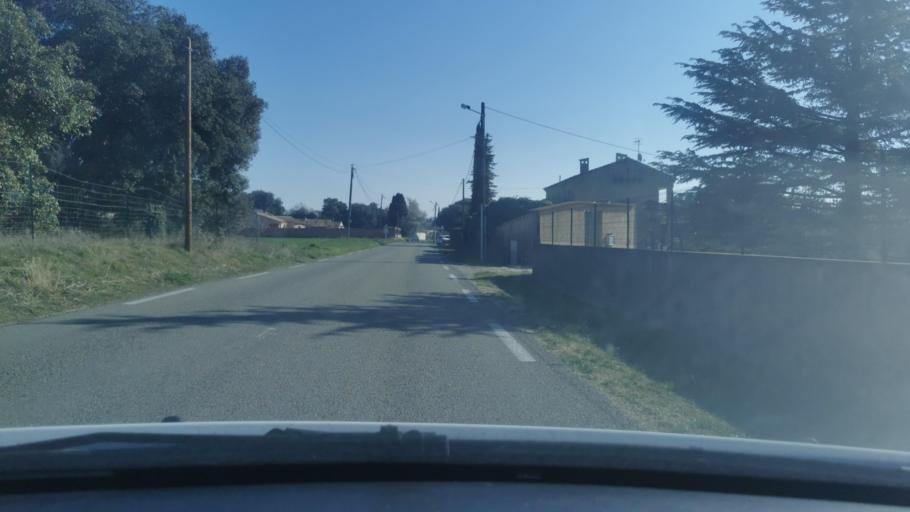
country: FR
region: Languedoc-Roussillon
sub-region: Departement du Gard
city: Saint-Quentin-la-Poterie
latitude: 44.0492
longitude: 4.4218
